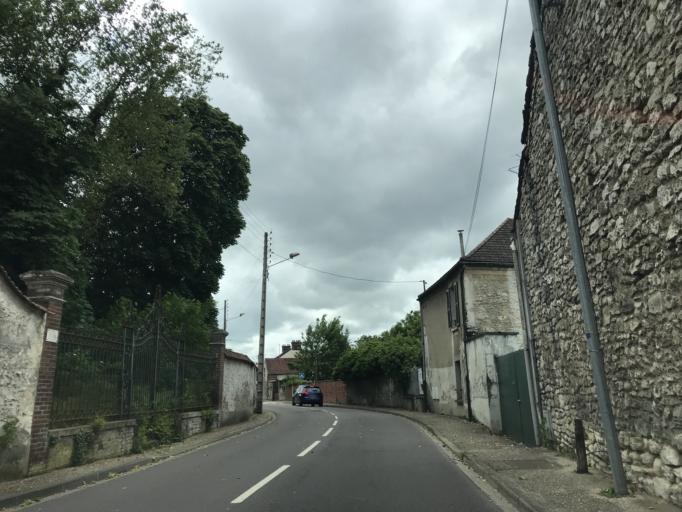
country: FR
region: Ile-de-France
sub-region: Departement des Yvelines
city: Rosny-sur-Seine
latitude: 49.0005
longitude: 1.6283
